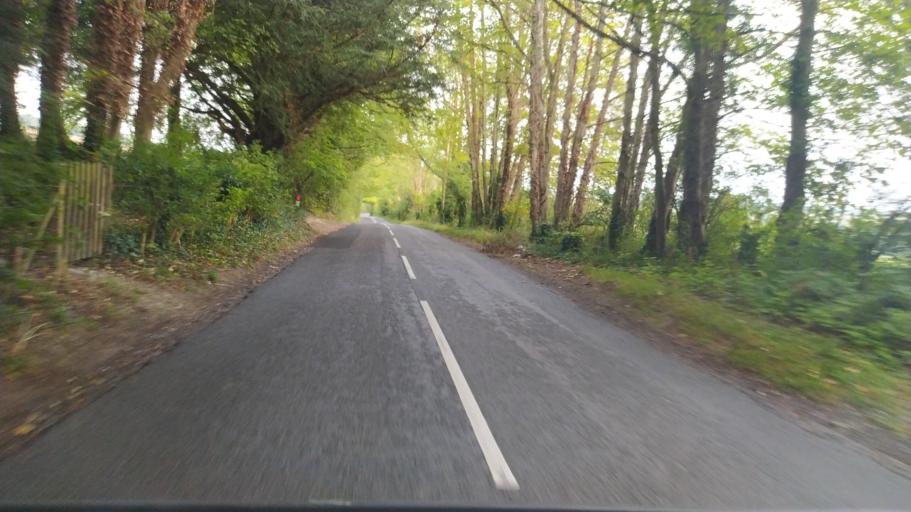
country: GB
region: England
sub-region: Hampshire
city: East Dean
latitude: 51.0841
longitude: -1.5623
